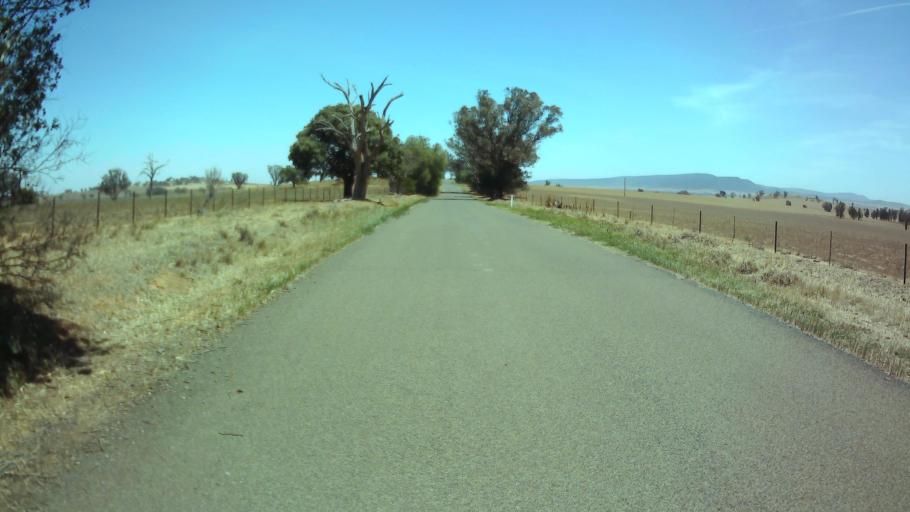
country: AU
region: New South Wales
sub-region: Weddin
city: Grenfell
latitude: -34.0552
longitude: 148.2339
